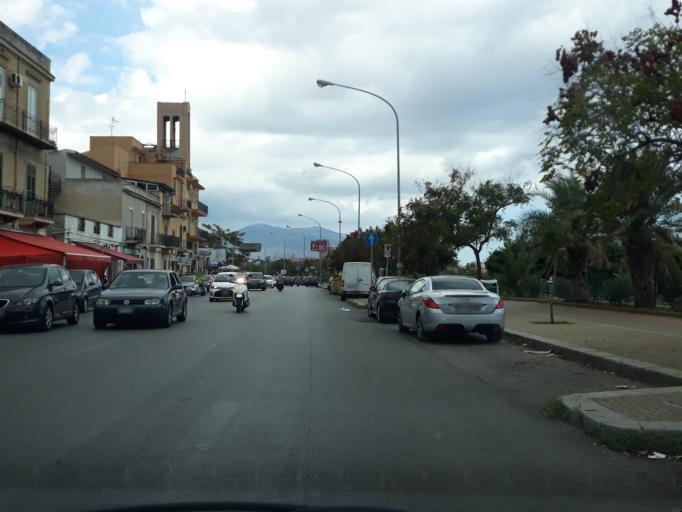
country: IT
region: Sicily
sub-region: Palermo
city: Ciaculli
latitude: 38.1051
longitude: 13.3894
